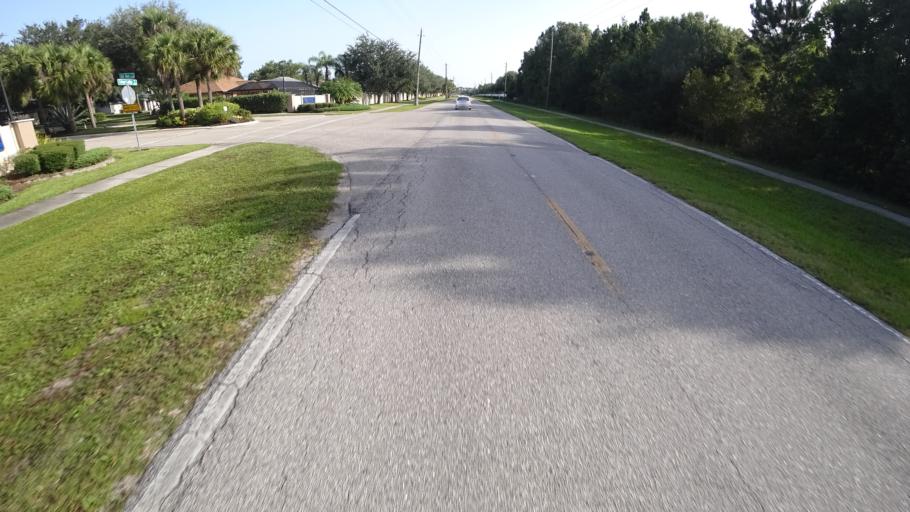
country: US
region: Florida
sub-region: Sarasota County
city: Desoto Lakes
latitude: 27.4232
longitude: -82.4709
